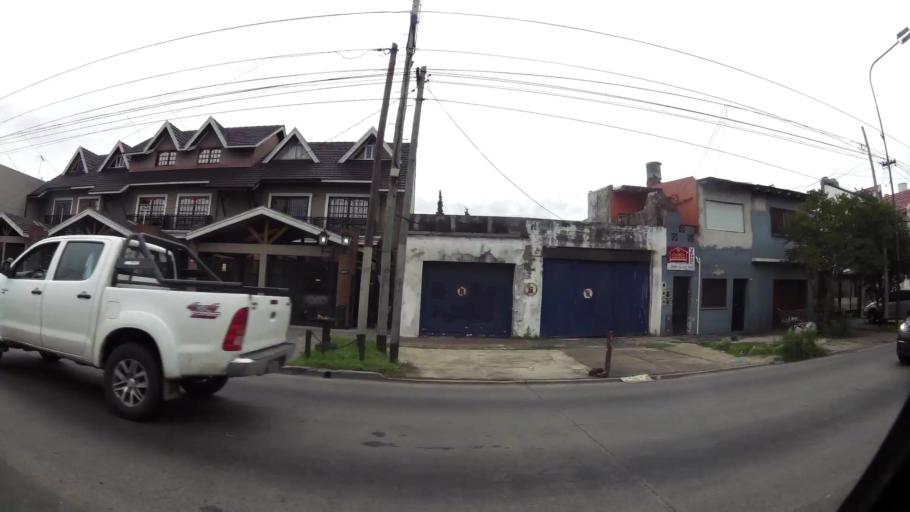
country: AR
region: Buenos Aires
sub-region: Partido de Lanus
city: Lanus
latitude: -34.7011
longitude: -58.3781
